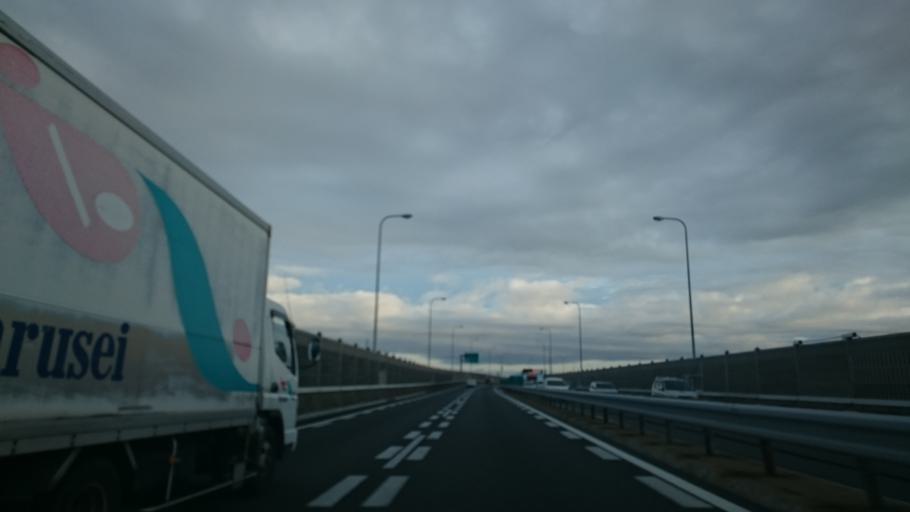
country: JP
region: Aichi
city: Kanie
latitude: 35.1940
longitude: 136.8164
